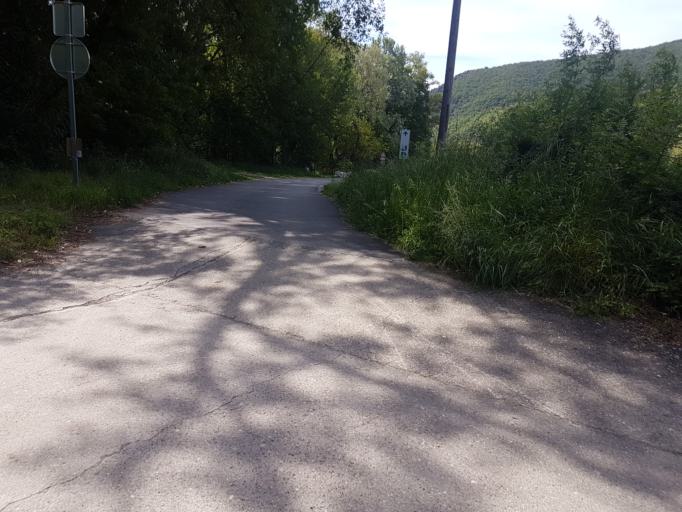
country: FR
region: Rhone-Alpes
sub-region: Departement de la Drome
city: Saulce-sur-Rhone
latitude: 44.7071
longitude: 4.7676
